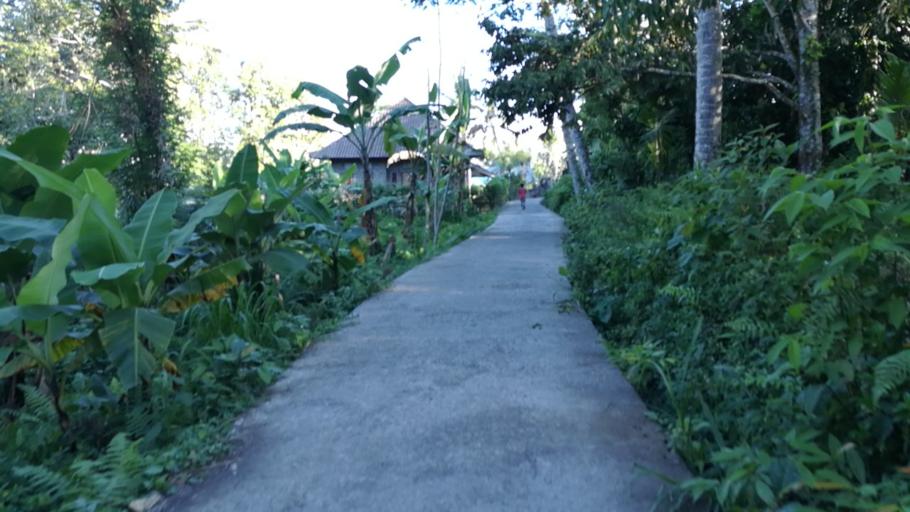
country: ID
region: Bali
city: Banjar Wangsian
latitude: -8.4334
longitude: 115.4292
